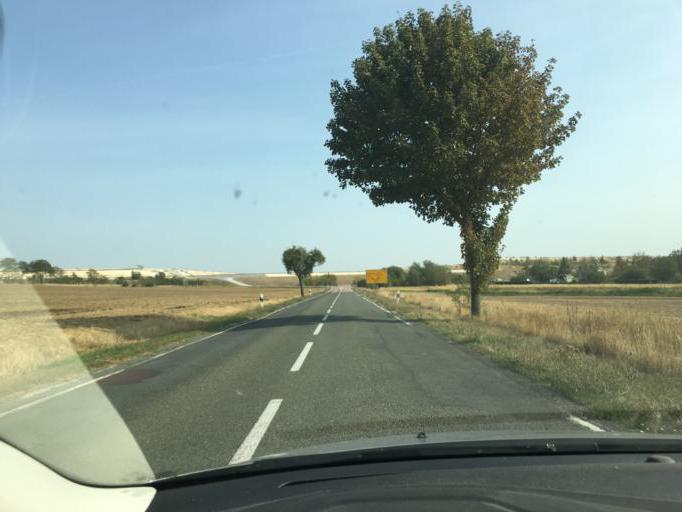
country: DE
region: Saxony-Anhalt
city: Nienburg/Saale
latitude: 51.8279
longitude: 11.8121
